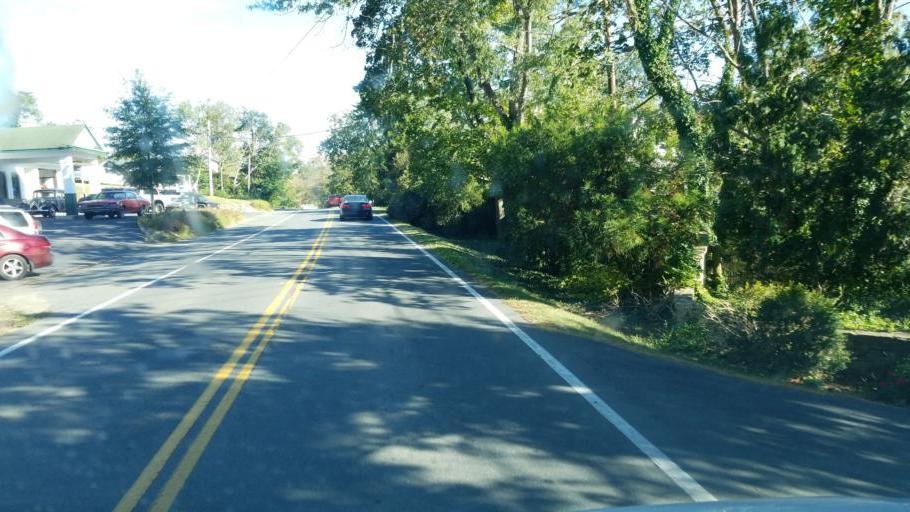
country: US
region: Virginia
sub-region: Prince William County
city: Bull Run Mountain Estates
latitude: 38.9772
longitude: -77.6486
